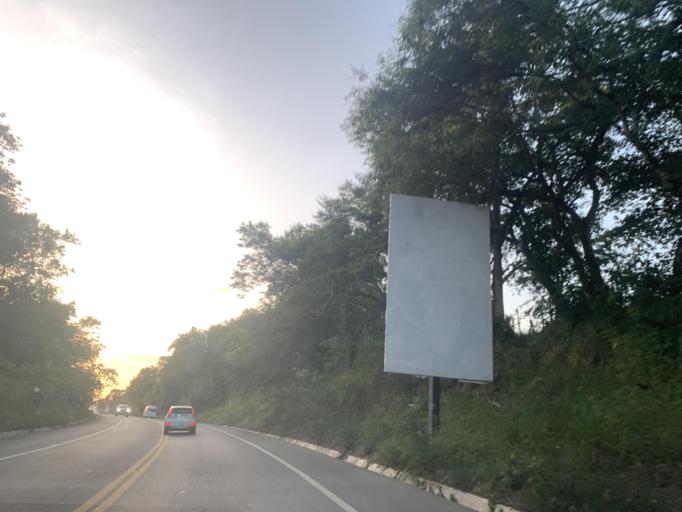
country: DO
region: Puerto Plata
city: Imbert
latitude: 19.7683
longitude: -70.8366
